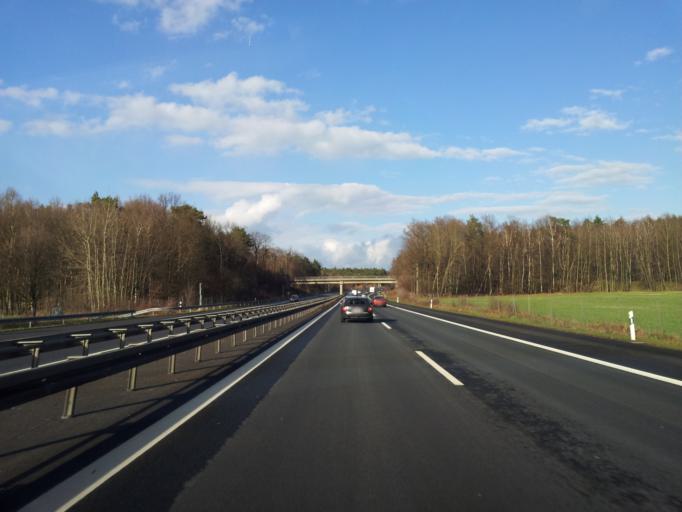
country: DE
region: Saxony
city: Albertstadt
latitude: 51.1417
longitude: 13.7600
